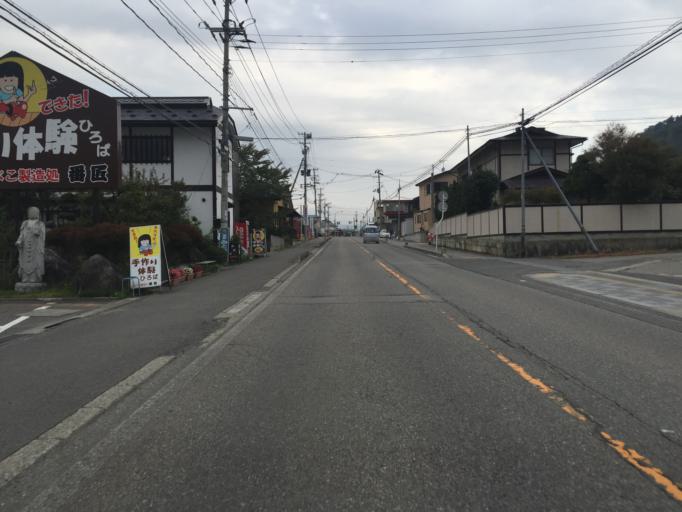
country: JP
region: Fukushima
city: Kitakata
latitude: 37.4987
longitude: 139.9502
